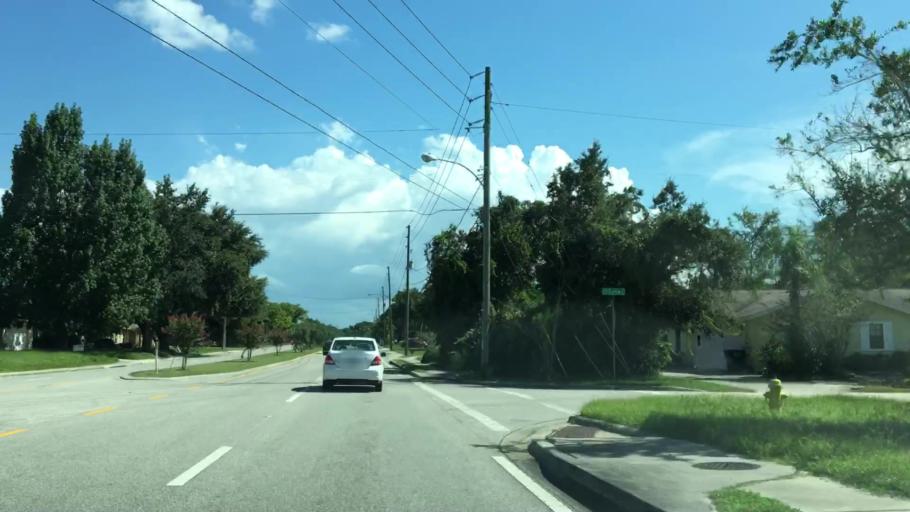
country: US
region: Florida
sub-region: Volusia County
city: Deltona
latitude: 28.9223
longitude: -81.2575
